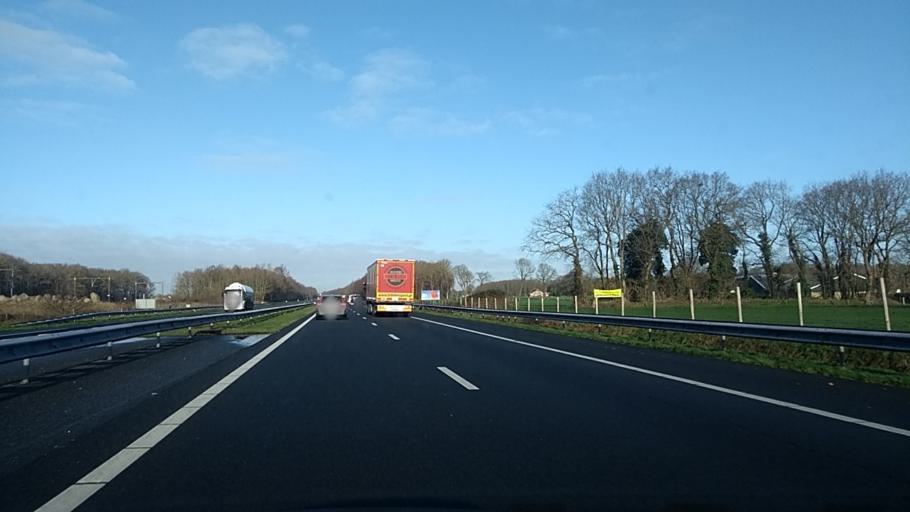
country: NL
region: Friesland
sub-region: Gemeente Weststellingwerf
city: Steggerda
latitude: 52.8370
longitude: 6.0563
